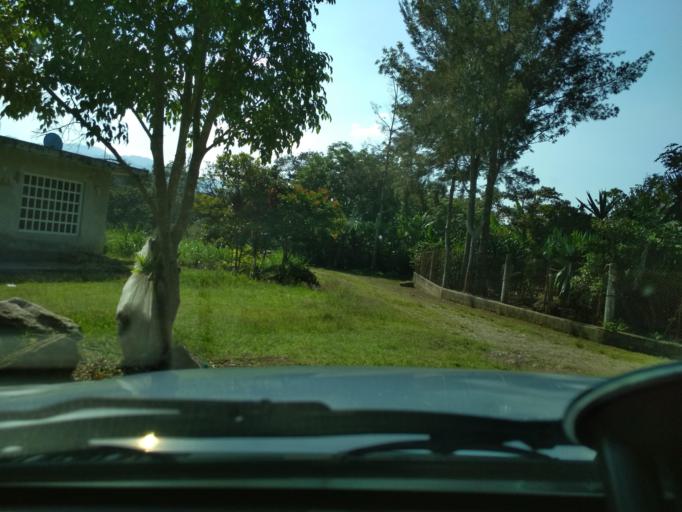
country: MX
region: Veracruz
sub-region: Chocaman
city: San Jose Neria
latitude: 18.9947
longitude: -96.9986
